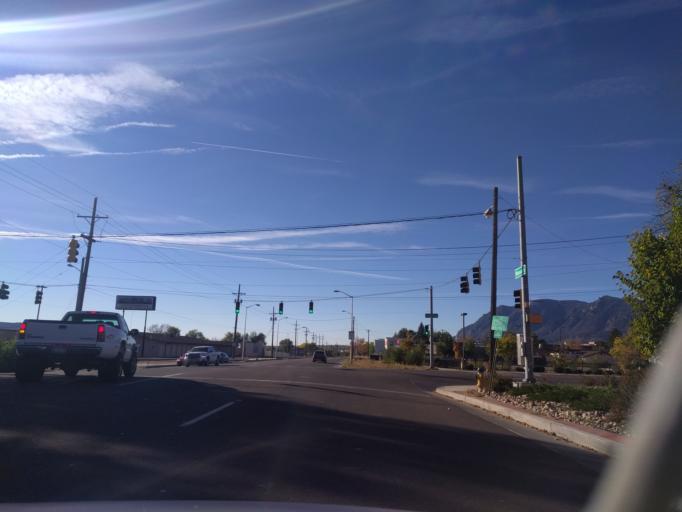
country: US
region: Colorado
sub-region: El Paso County
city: Colorado Springs
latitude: 38.8285
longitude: -104.8185
